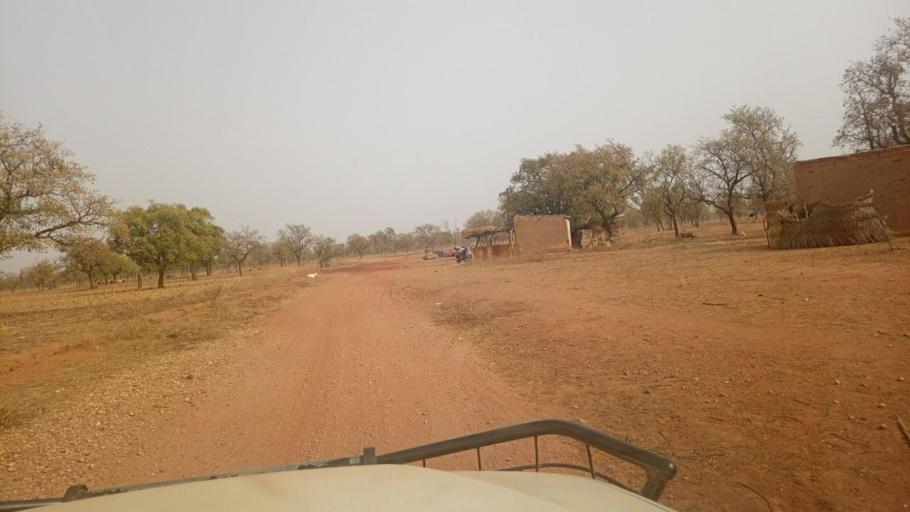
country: BF
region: Boucle du Mouhoun
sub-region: Province des Banwa
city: Salanso
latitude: 12.0944
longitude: -4.3293
